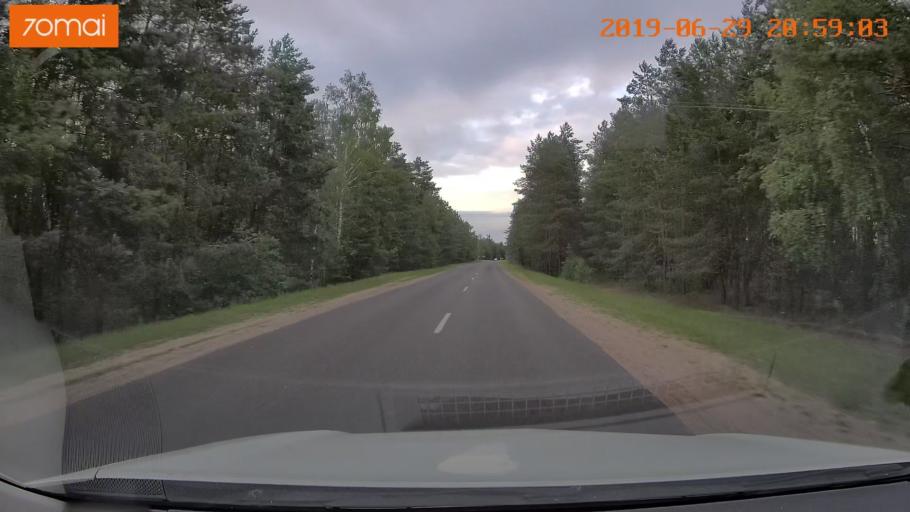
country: BY
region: Brest
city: Hantsavichy
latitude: 52.7347
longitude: 26.3981
